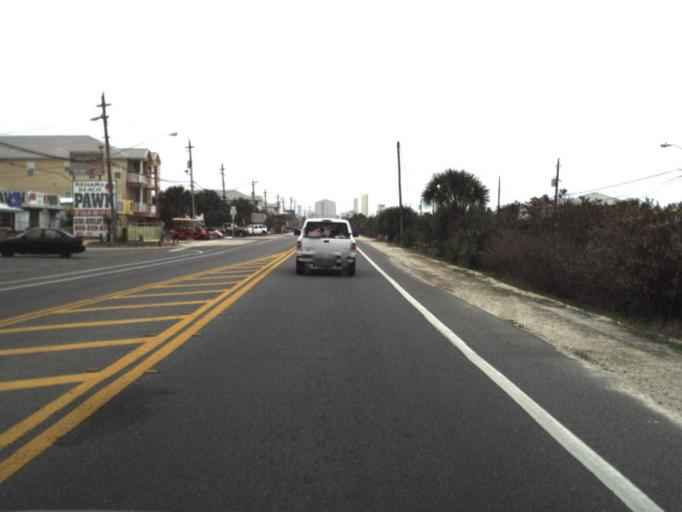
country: US
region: Florida
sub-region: Bay County
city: Panama City Beach
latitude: 30.1985
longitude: -85.8450
